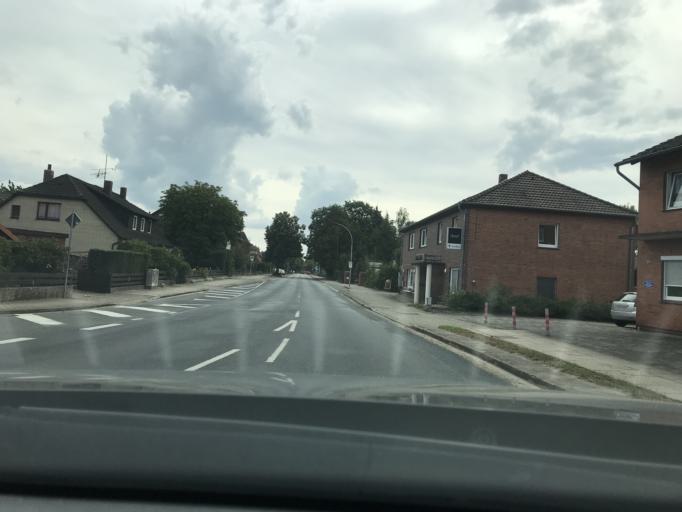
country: DE
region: Lower Saxony
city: Suderburg
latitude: 52.9043
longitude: 10.4355
